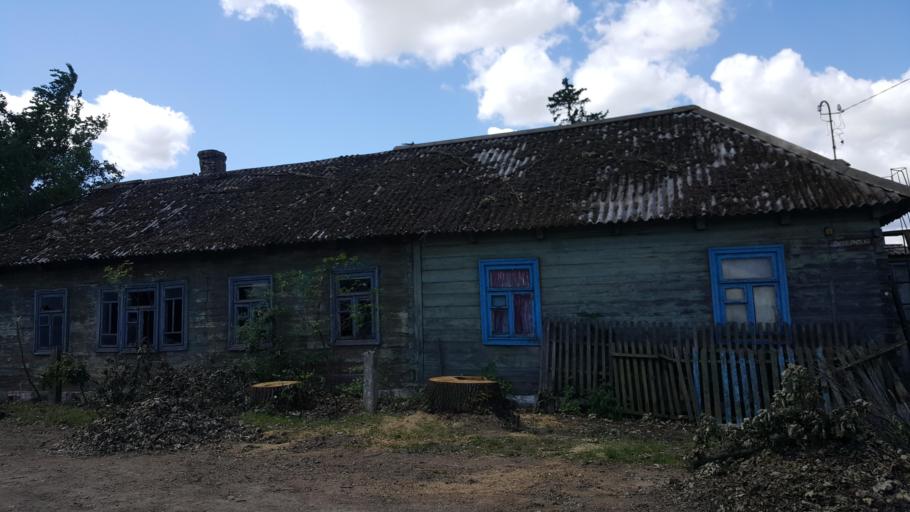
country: BY
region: Brest
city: Kamyanyets
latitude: 52.3227
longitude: 23.9159
